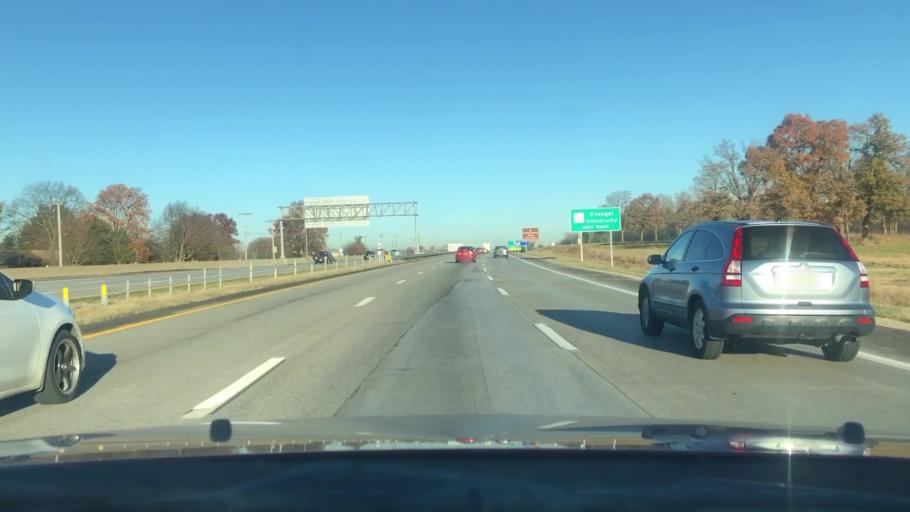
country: US
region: Missouri
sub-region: Greene County
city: Springfield
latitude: 37.1332
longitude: -93.2449
